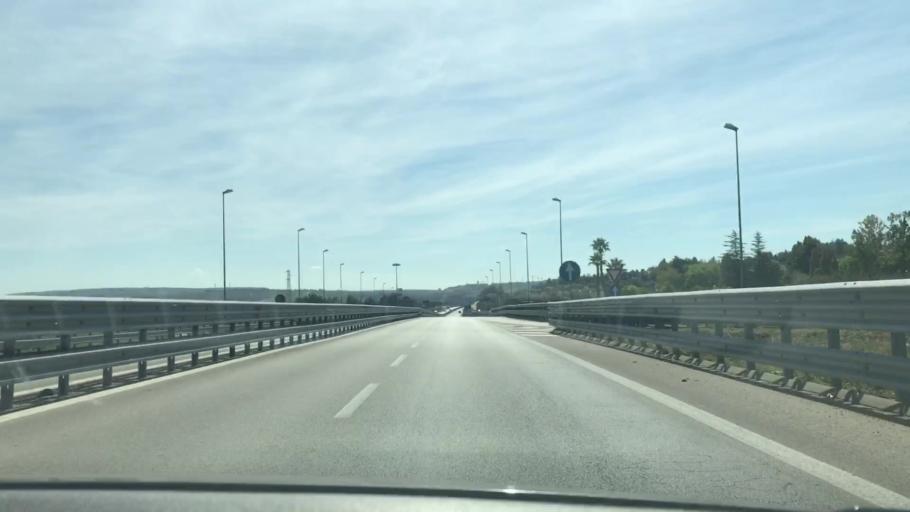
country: IT
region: Basilicate
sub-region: Provincia di Matera
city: Matera
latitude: 40.7019
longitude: 16.5861
